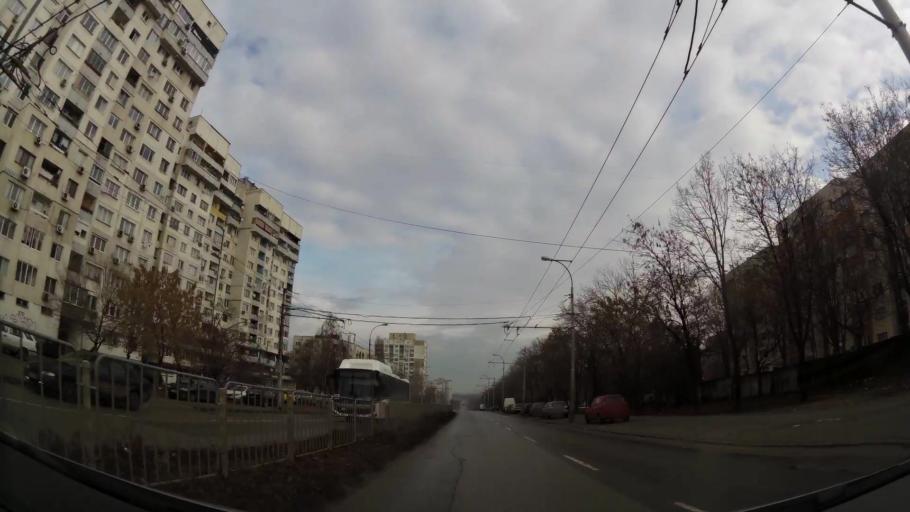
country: BG
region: Sofiya
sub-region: Obshtina Bozhurishte
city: Bozhurishte
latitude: 42.7218
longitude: 23.2413
